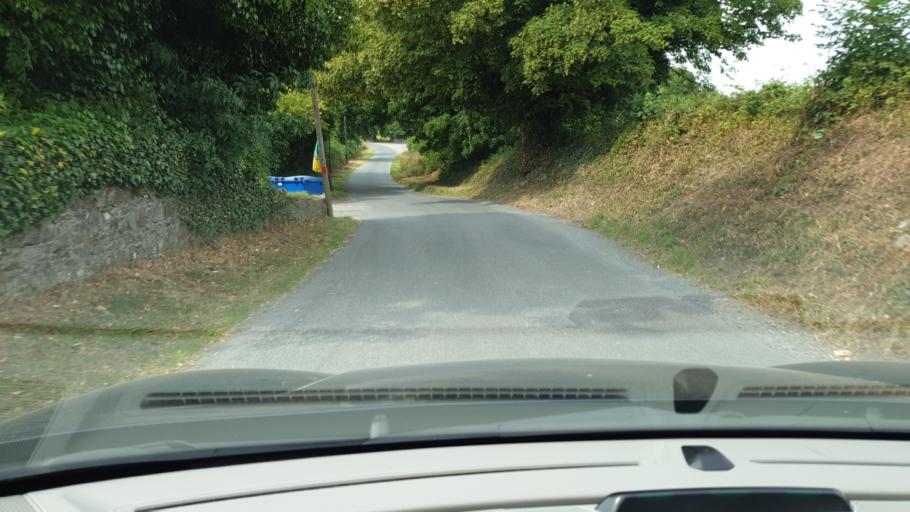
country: IE
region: Leinster
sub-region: An Mhi
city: Athboy
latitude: 53.6663
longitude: -6.9208
